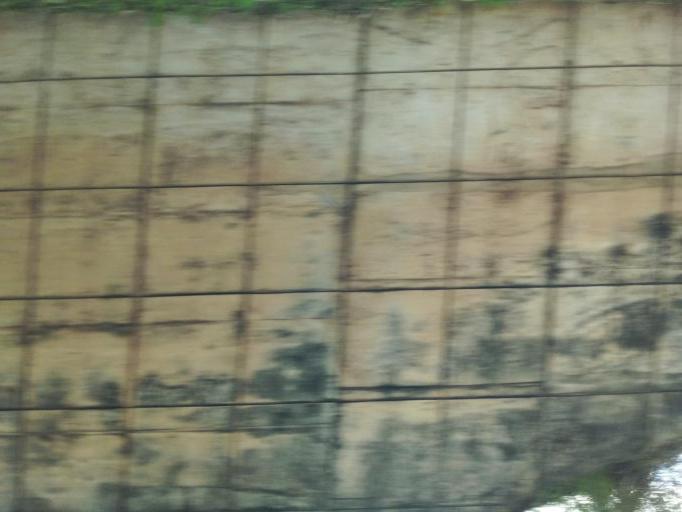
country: BR
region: Minas Gerais
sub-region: Governador Valadares
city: Governador Valadares
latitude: -18.9136
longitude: -42.0044
